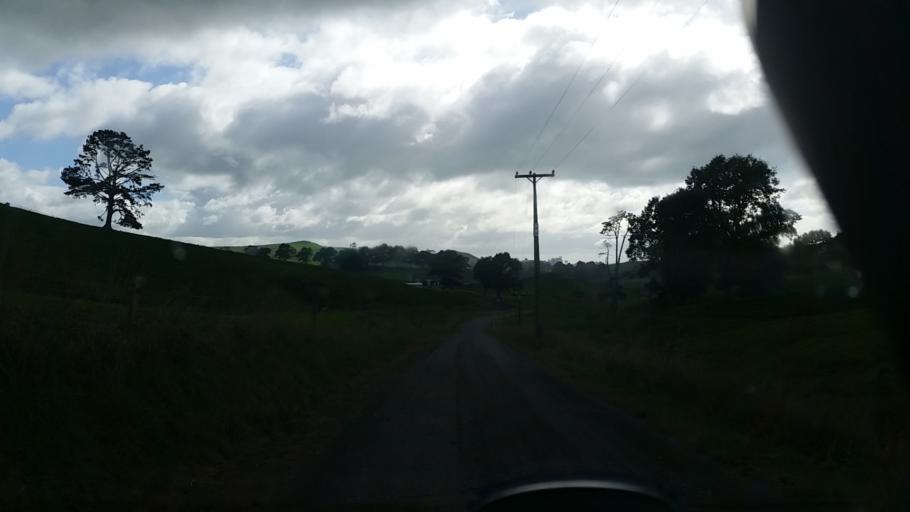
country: NZ
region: Waikato
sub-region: Matamata-Piako District
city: Matamata
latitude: -37.8174
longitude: 175.6740
